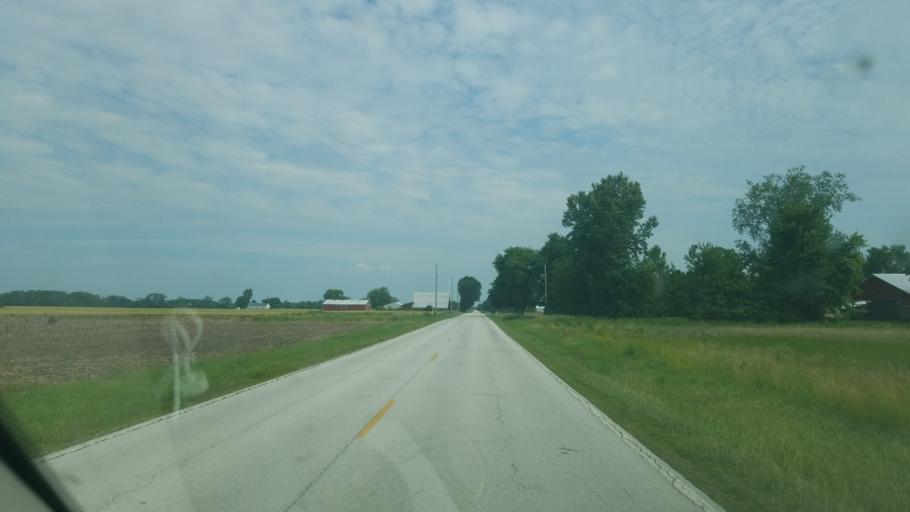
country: US
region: Ohio
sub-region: Seneca County
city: Fostoria
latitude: 41.0847
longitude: -83.4783
